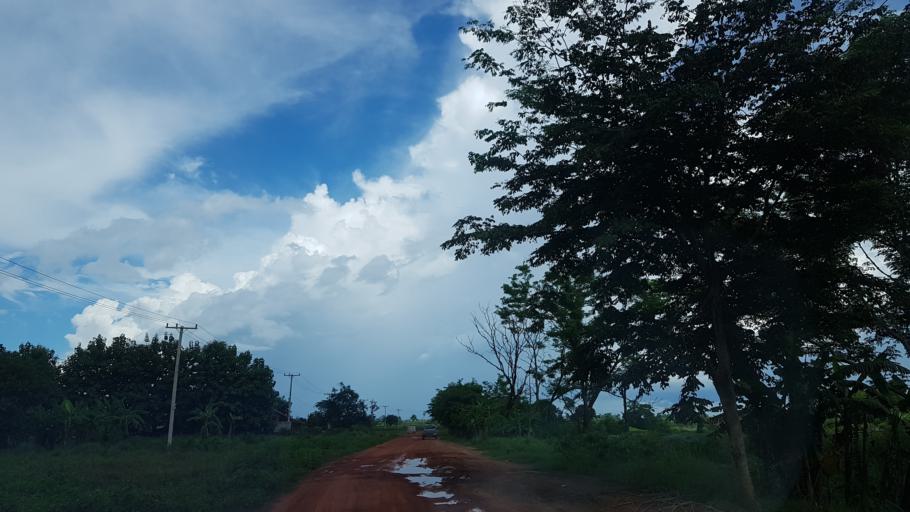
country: LA
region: Vientiane
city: Vientiane
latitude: 18.2368
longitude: 102.5595
